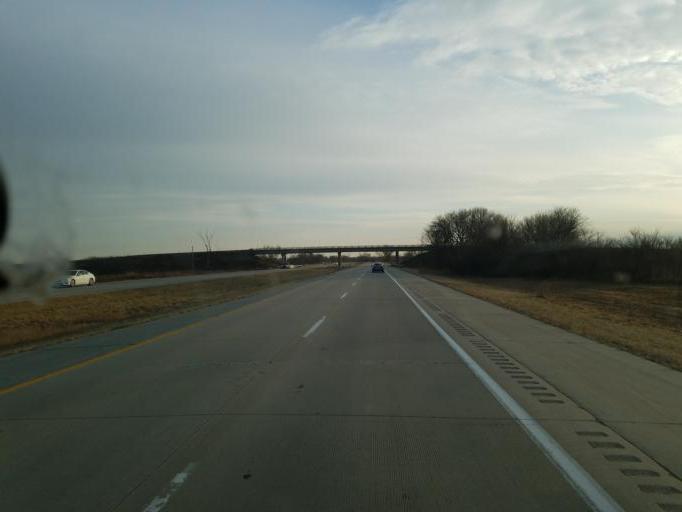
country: US
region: Nebraska
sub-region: Burt County
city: Tekamah
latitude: 41.8592
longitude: -96.1026
